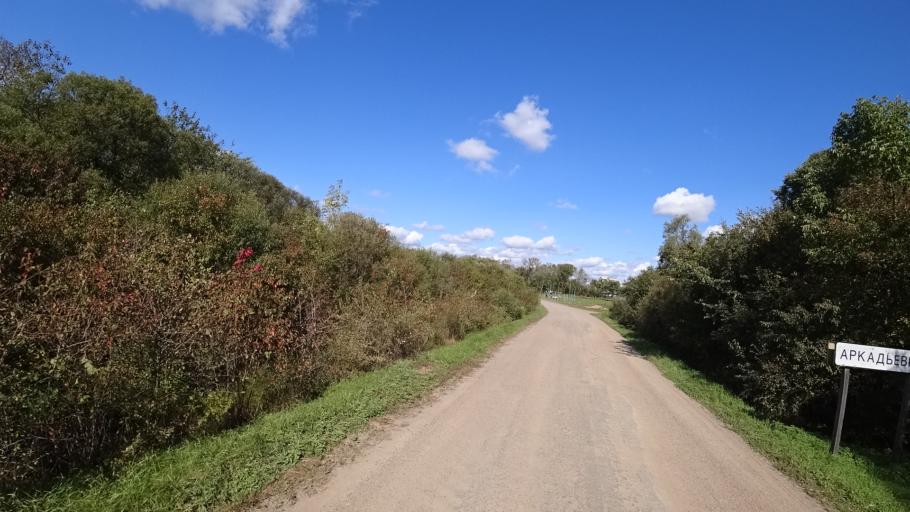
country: RU
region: Amur
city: Arkhara
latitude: 49.4001
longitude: 130.1373
